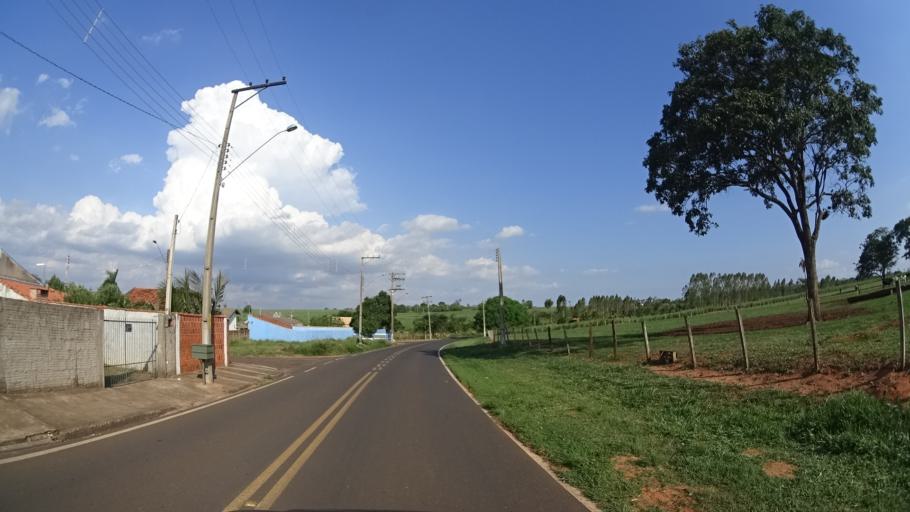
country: BR
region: Sao Paulo
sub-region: Urupes
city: Urupes
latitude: -21.3641
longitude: -49.4770
